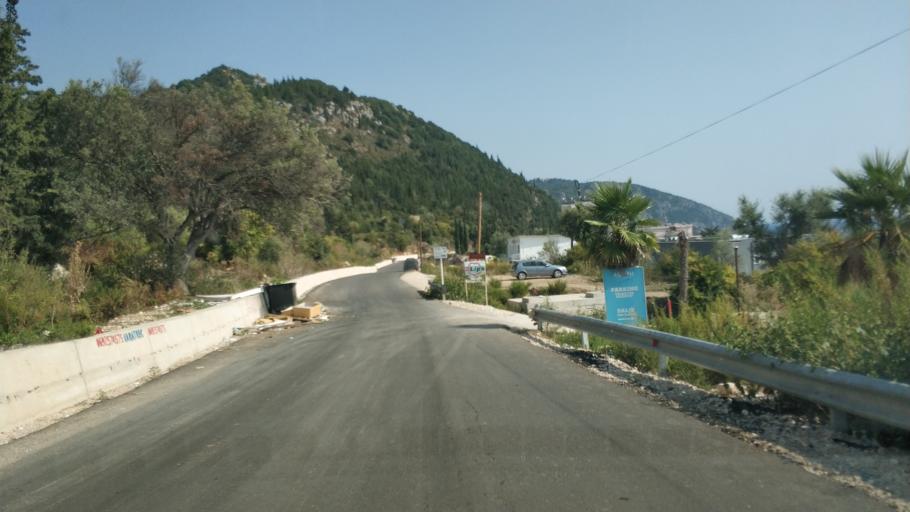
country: AL
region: Vlore
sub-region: Rrethi i Vlores
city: Vranisht
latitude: 40.1435
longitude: 19.6389
